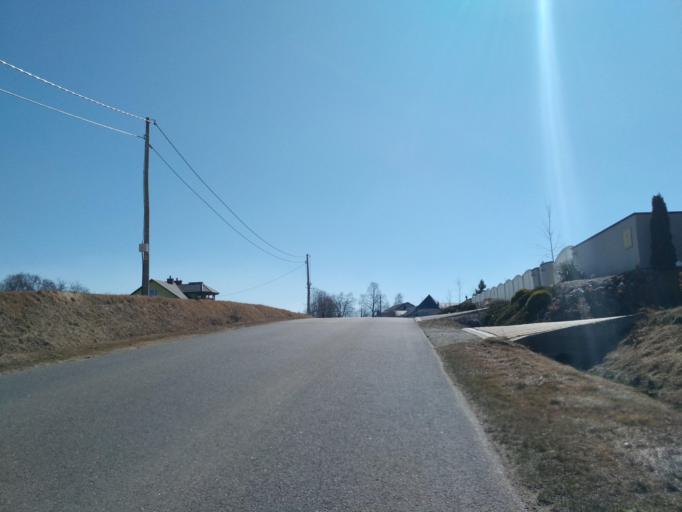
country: PL
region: Subcarpathian Voivodeship
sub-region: Powiat ropczycko-sedziszowski
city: Niedzwiada
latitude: 49.9502
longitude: 21.4879
